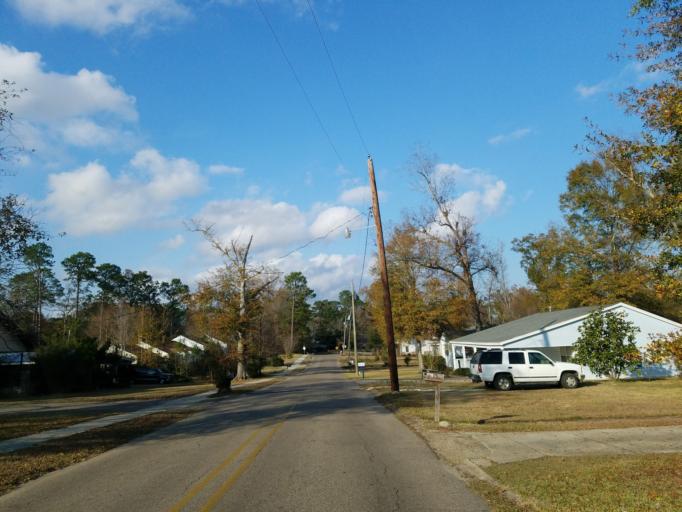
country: US
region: Mississippi
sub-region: Forrest County
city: Hattiesburg
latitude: 31.3269
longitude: -89.3228
